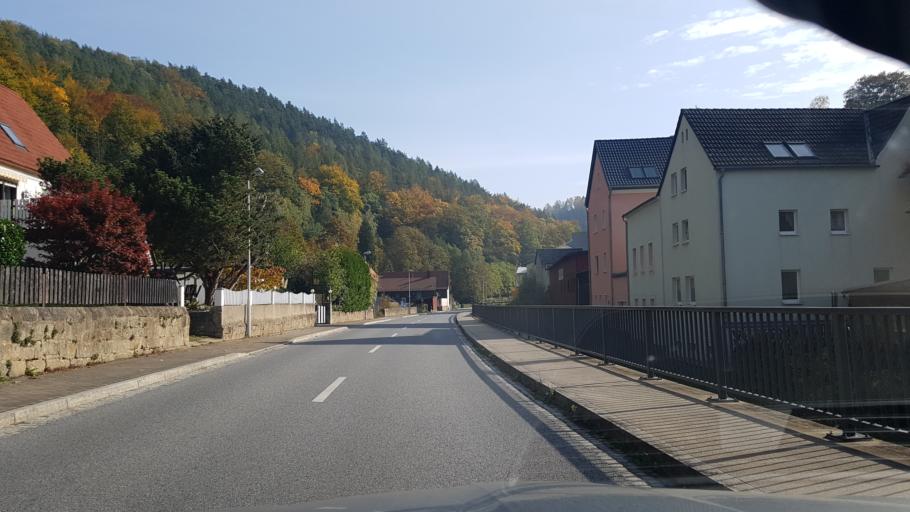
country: DE
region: Saxony
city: Konigstein
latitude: 50.9145
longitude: 14.0612
